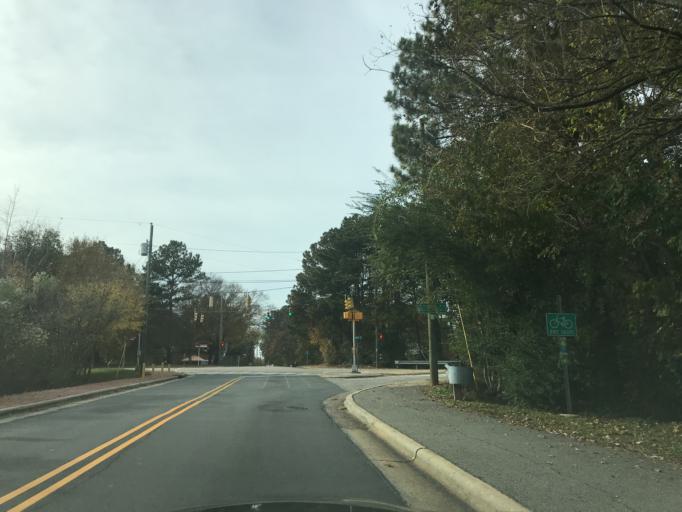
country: US
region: North Carolina
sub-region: Wake County
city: West Raleigh
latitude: 35.7890
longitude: -78.6857
